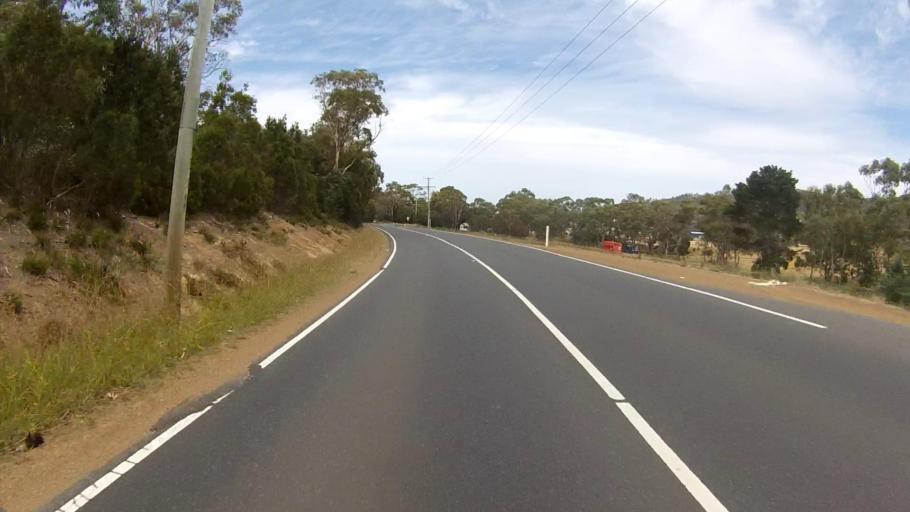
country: AU
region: Tasmania
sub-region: Clarence
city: Acton Park
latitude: -42.8732
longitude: 147.4828
